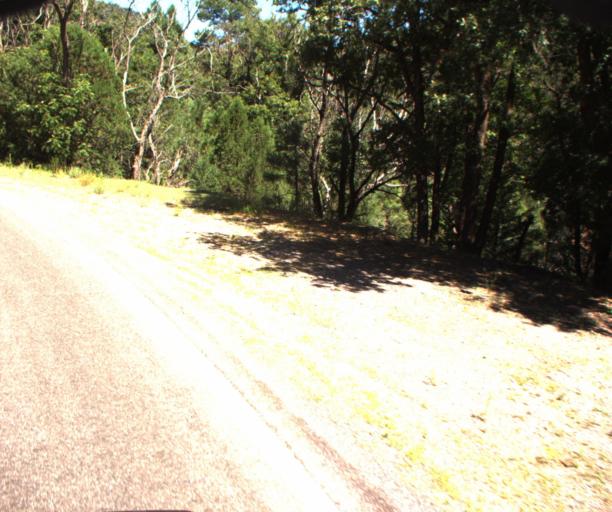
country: US
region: Arizona
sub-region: Greenlee County
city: Morenci
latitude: 33.1821
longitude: -109.3799
